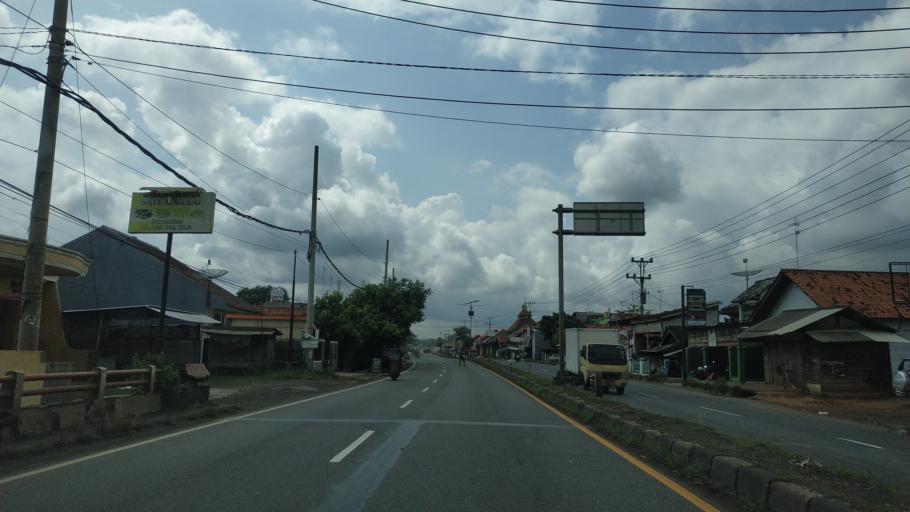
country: ID
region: Central Java
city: Pekalongan
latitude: -6.9517
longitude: 109.8020
